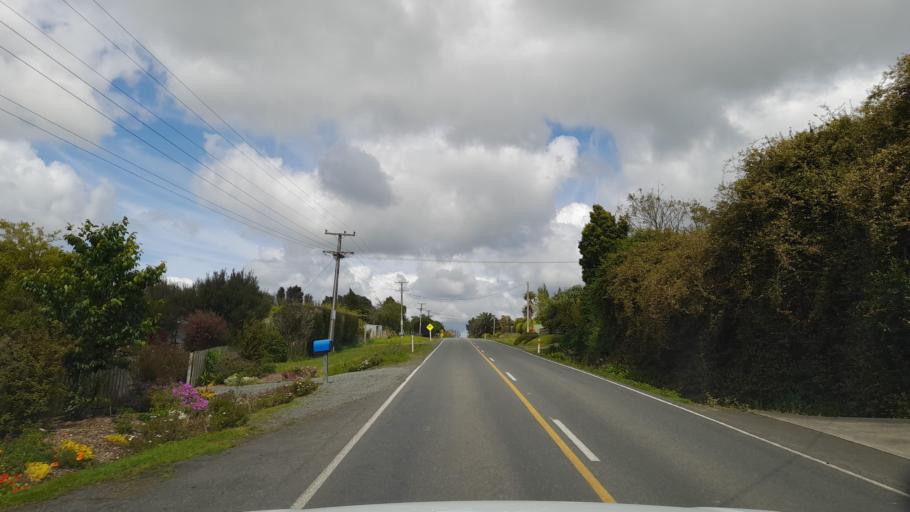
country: NZ
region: Northland
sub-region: Whangarei
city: Maungatapere
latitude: -35.6584
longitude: 174.1774
